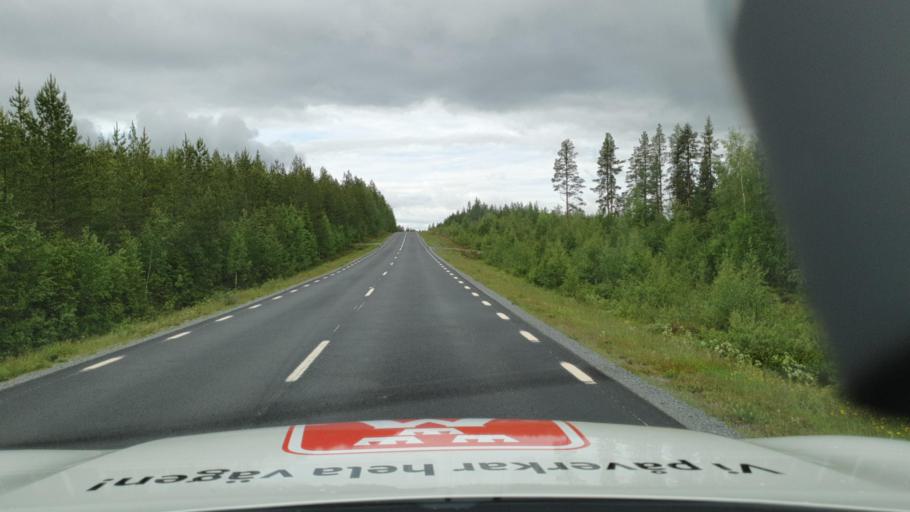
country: SE
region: Vaesterbotten
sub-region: Dorotea Kommun
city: Dorotea
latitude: 64.1900
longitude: 16.6074
